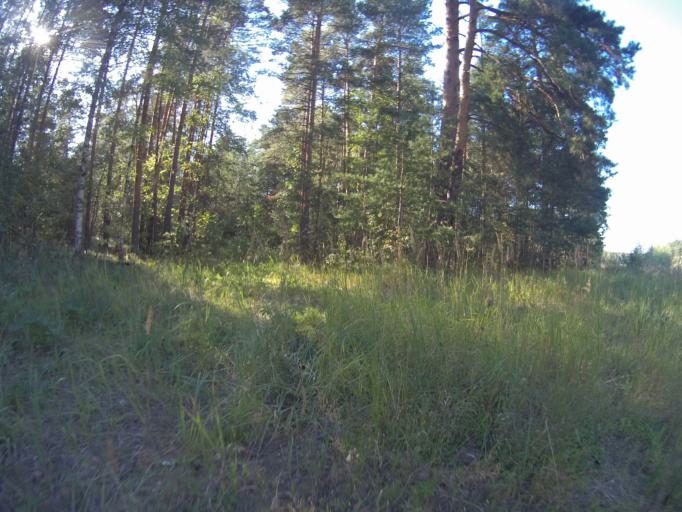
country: RU
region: Vladimir
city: Kommunar
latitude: 56.0611
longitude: 40.4336
